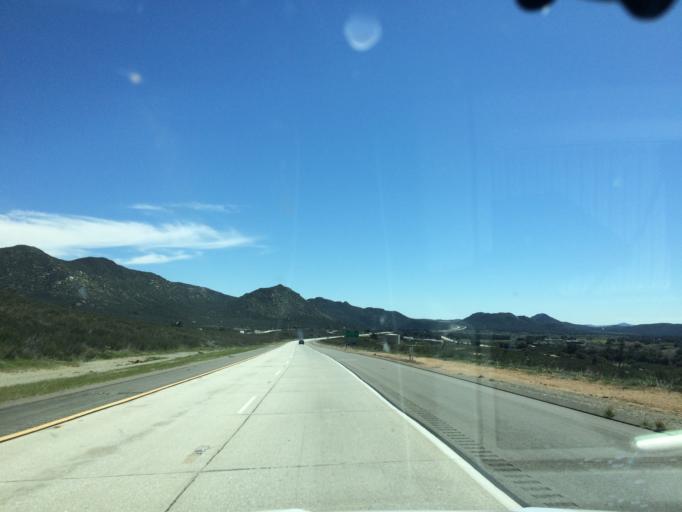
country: US
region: California
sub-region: San Diego County
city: Pine Valley
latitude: 32.7717
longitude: -116.4913
